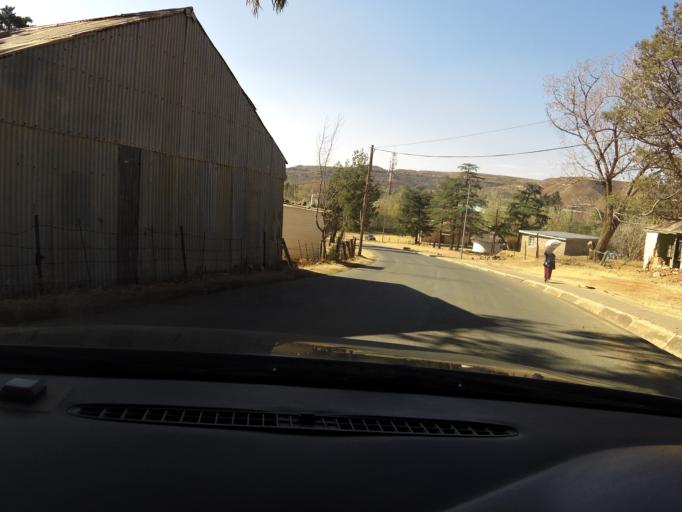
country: LS
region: Mohale's Hoek District
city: Mohale's Hoek
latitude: -30.1534
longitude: 27.4754
